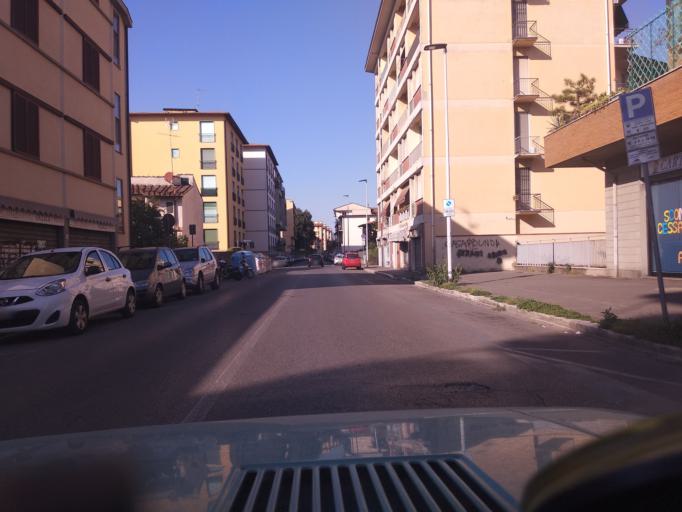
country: IT
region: Tuscany
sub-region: Province of Florence
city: Florence
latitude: 43.7754
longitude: 11.2142
